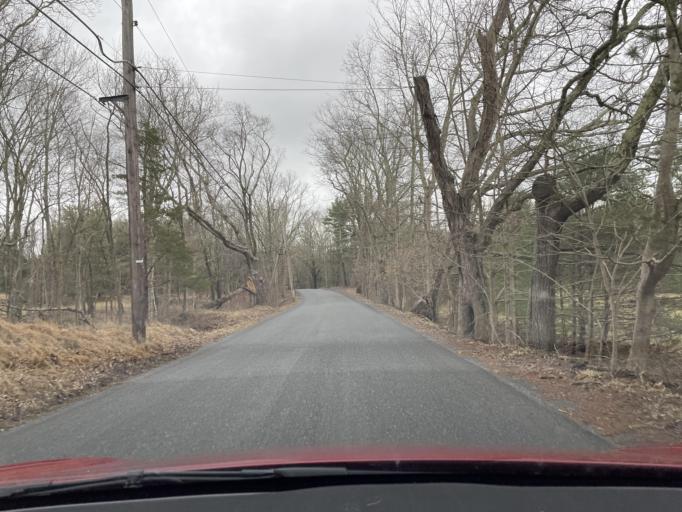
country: US
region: New York
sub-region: Ulster County
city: Manorville
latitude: 42.0860
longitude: -74.0357
